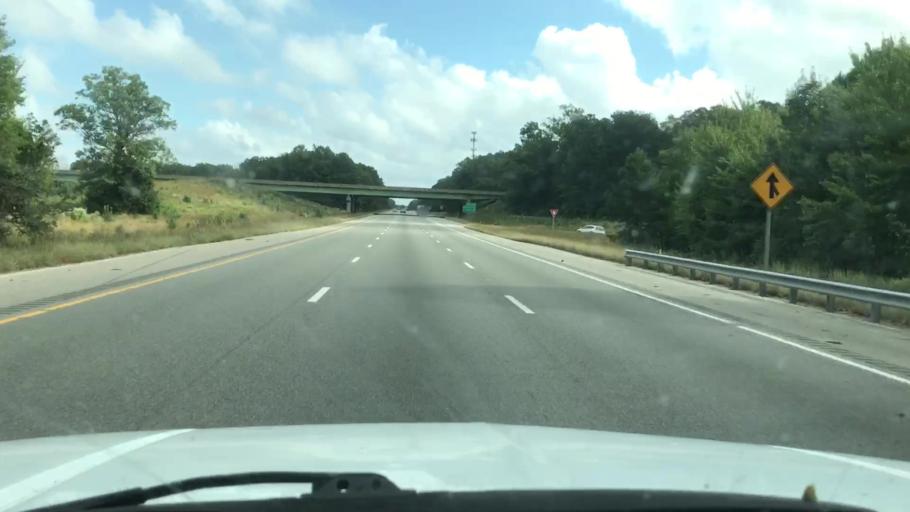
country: US
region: Virginia
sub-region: Henrico County
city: Short Pump
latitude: 37.6695
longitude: -77.5837
